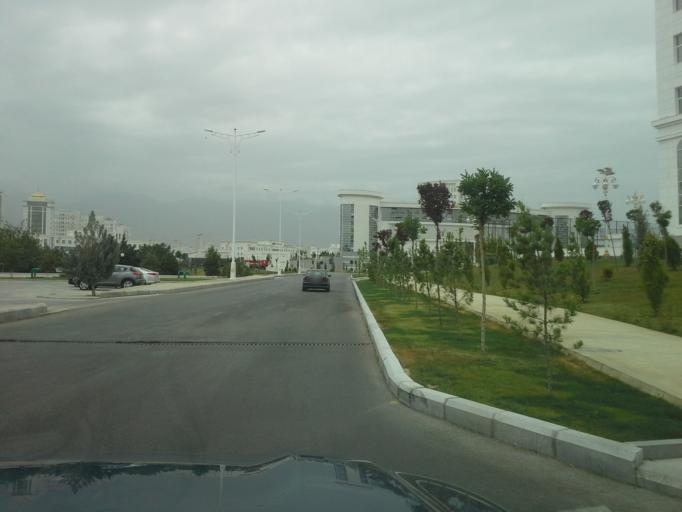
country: TM
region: Ahal
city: Ashgabat
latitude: 37.9186
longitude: 58.3711
